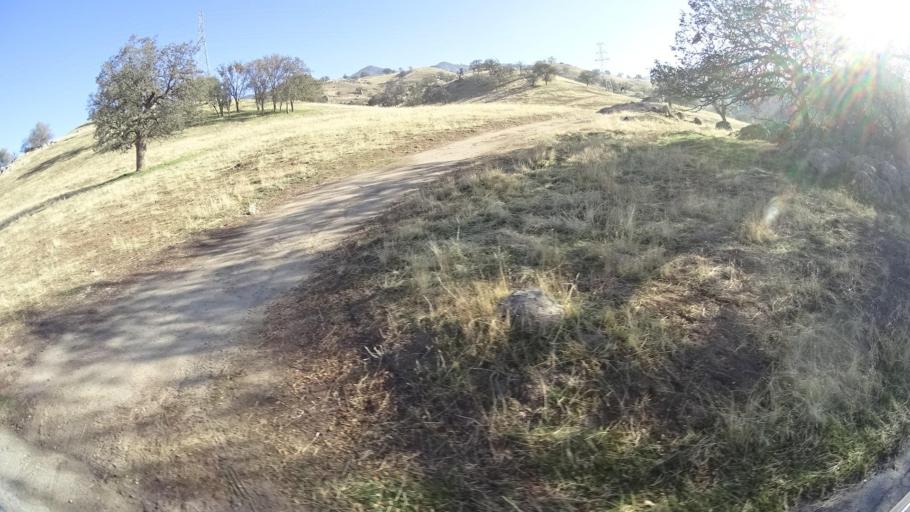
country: US
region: California
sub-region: Kern County
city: Alta Sierra
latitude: 35.7243
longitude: -118.8094
